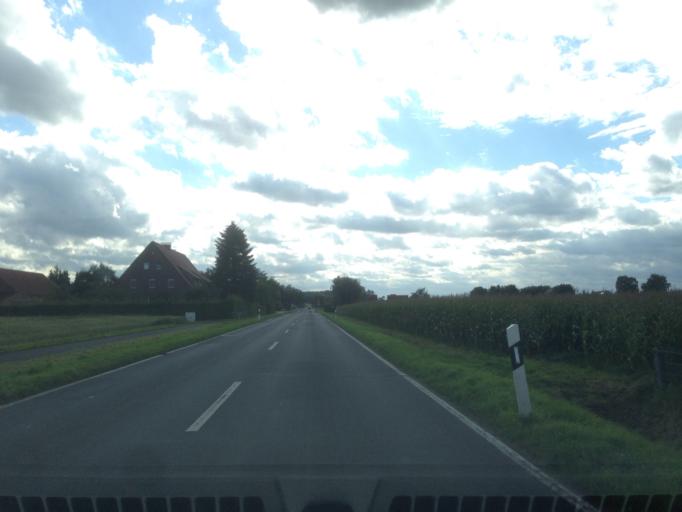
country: DE
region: North Rhine-Westphalia
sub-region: Regierungsbezirk Munster
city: Senden
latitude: 51.8177
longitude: 7.5036
